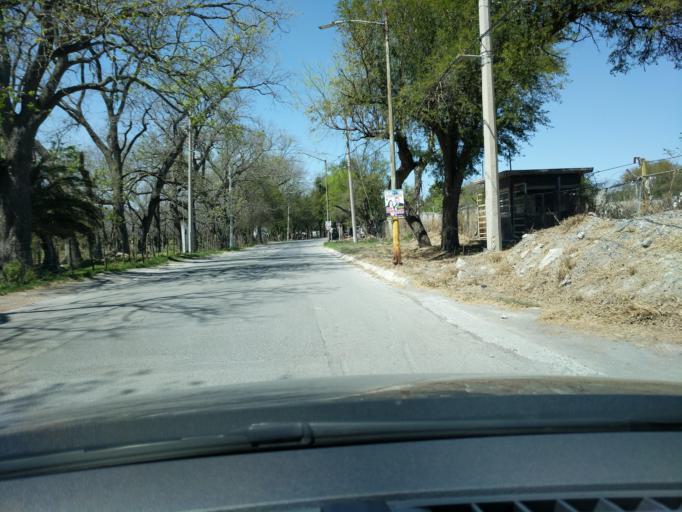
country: MX
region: Nuevo Leon
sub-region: Apodaca
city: Artemio Trevino
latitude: 25.8120
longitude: -100.1313
